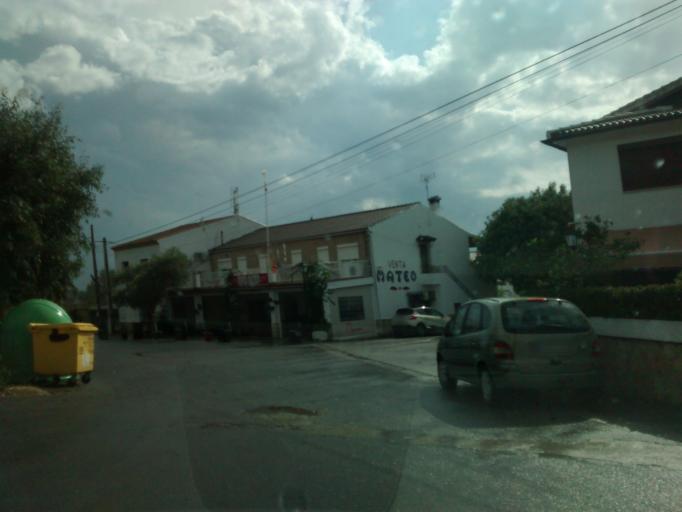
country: ES
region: Andalusia
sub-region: Provincia de Cadiz
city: El Bosque
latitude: 36.7522
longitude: -5.5067
